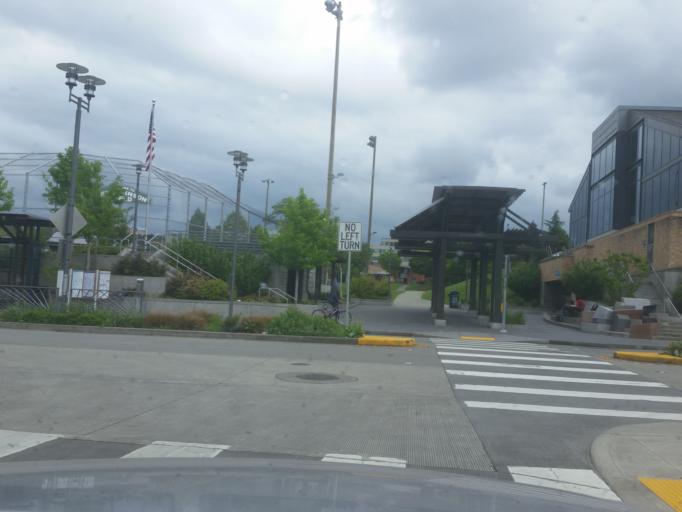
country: US
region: Washington
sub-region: King County
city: Kirkland
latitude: 47.6765
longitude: -122.2035
